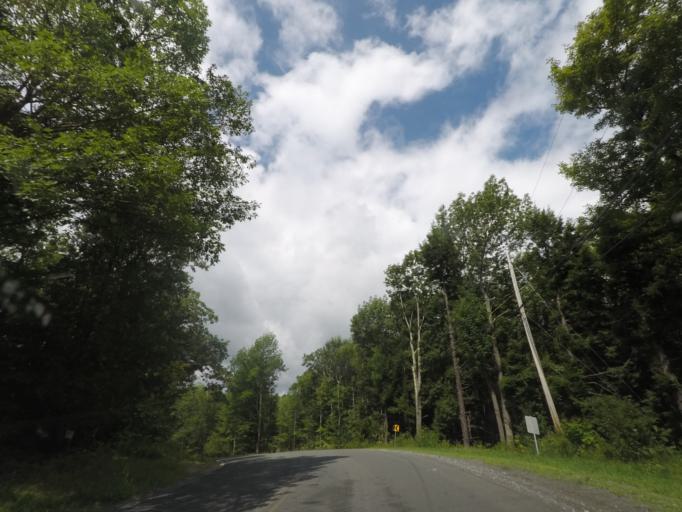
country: US
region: New York
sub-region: Rensselaer County
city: Poestenkill
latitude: 42.6992
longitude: -73.3936
